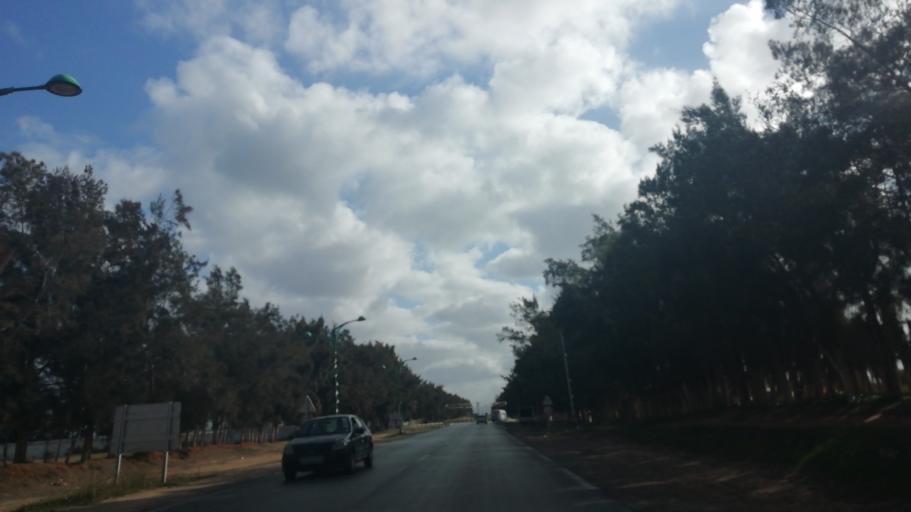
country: DZ
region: Relizane
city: Mazouna
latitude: 36.2552
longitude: 0.5809
